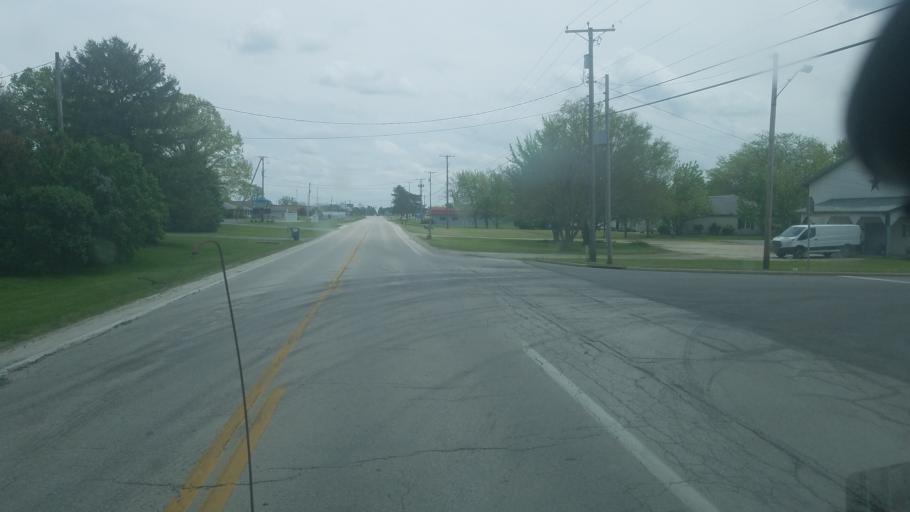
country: US
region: Ohio
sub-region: Seneca County
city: Tiffin
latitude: 41.0845
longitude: -83.1559
